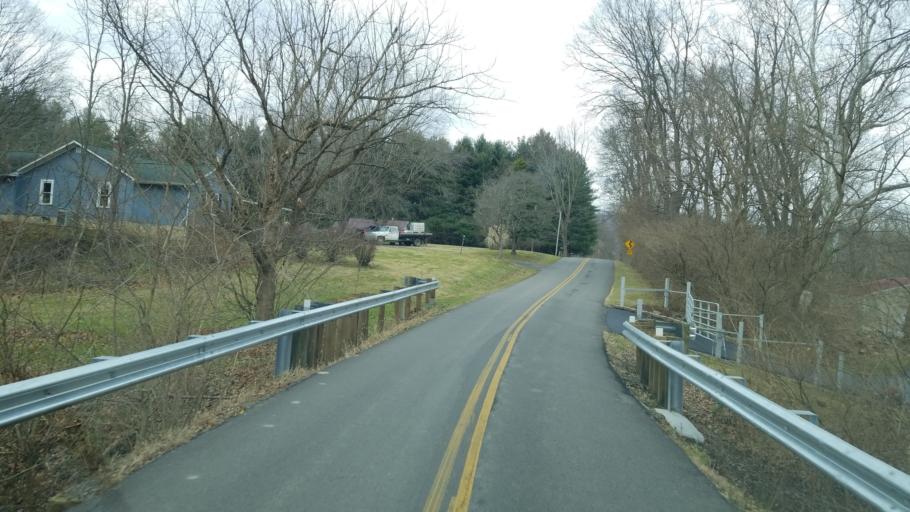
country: US
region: Ohio
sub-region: Highland County
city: Greenfield
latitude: 39.2342
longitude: -83.2890
